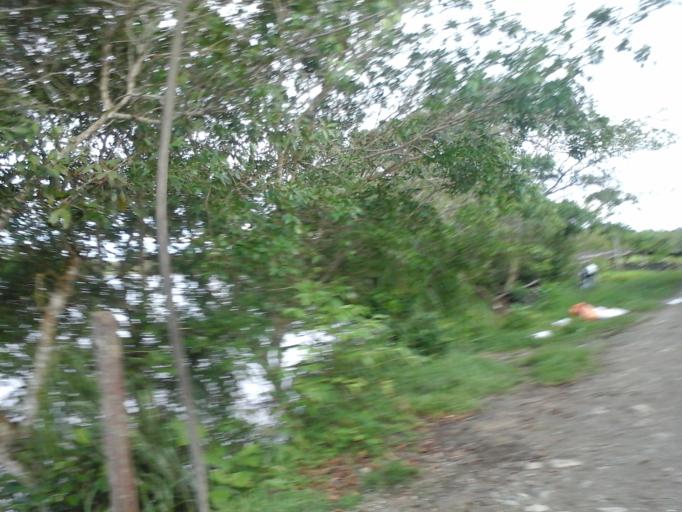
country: CO
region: Caqueta
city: El Doncello
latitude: 1.6117
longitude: -74.9938
